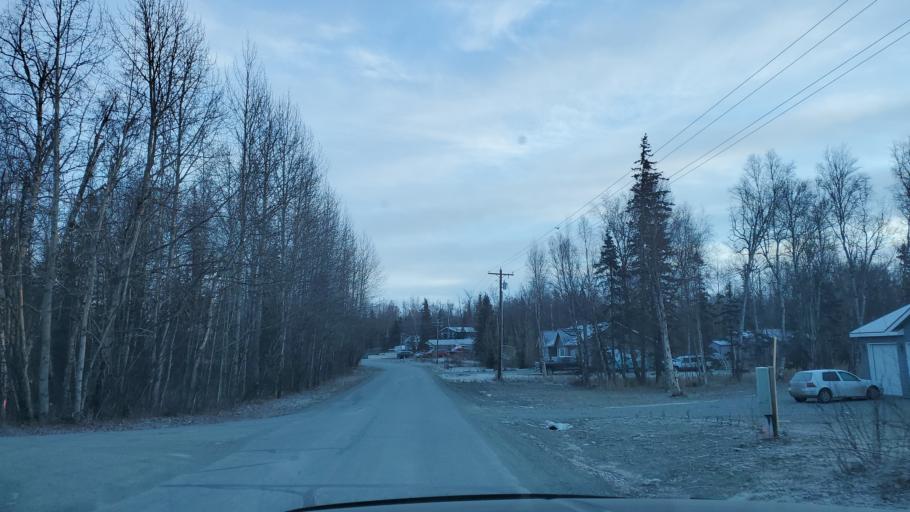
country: US
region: Alaska
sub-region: Matanuska-Susitna Borough
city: Lakes
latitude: 61.6080
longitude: -149.3136
